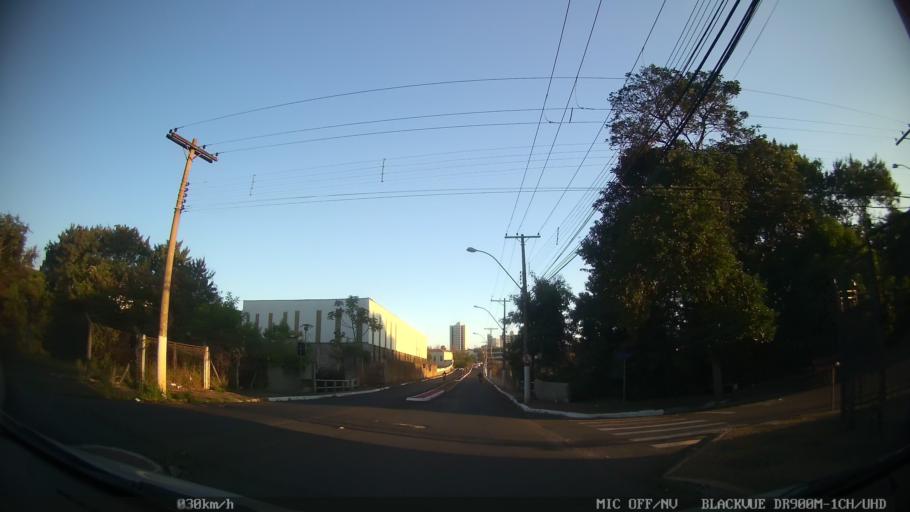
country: BR
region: Sao Paulo
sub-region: Santa Barbara D'Oeste
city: Santa Barbara d'Oeste
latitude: -22.7473
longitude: -47.4102
